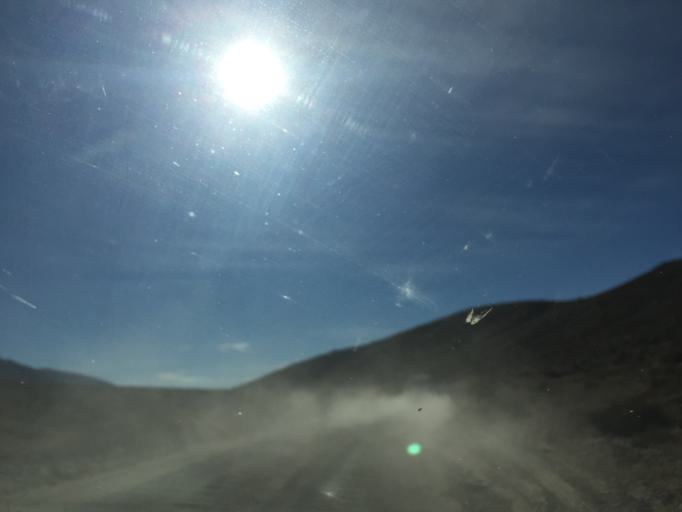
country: US
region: California
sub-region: Inyo County
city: Lone Pine
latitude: 36.8712
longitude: -117.4990
